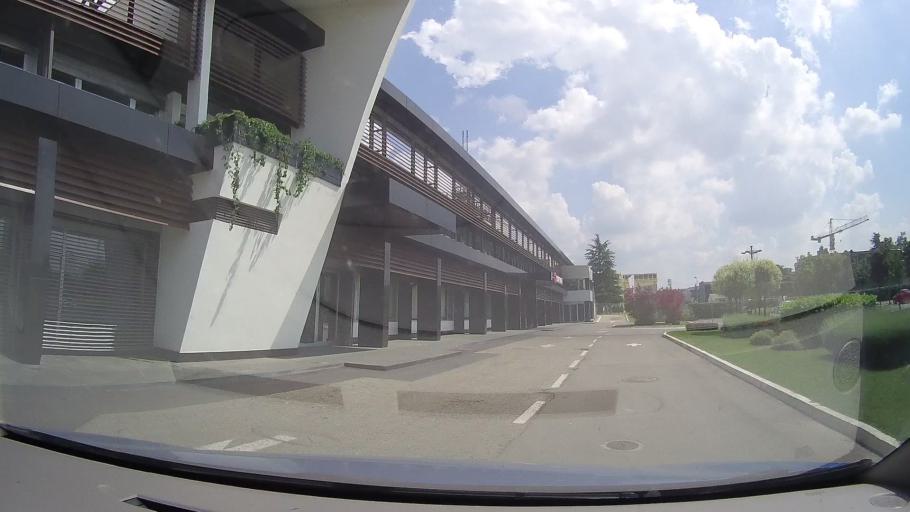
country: RS
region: Central Serbia
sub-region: Belgrade
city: Novi Beograd
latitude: 44.8021
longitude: 20.4193
